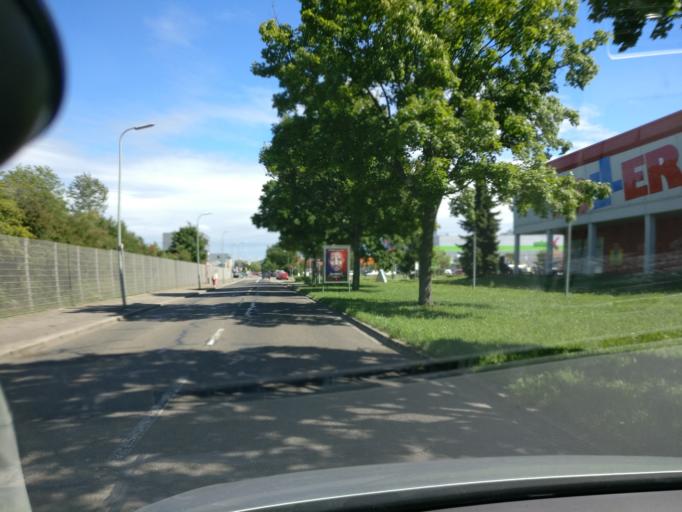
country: DE
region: Baden-Wuerttemberg
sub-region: Karlsruhe Region
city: Karlsruhe
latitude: 49.0213
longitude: 8.4558
